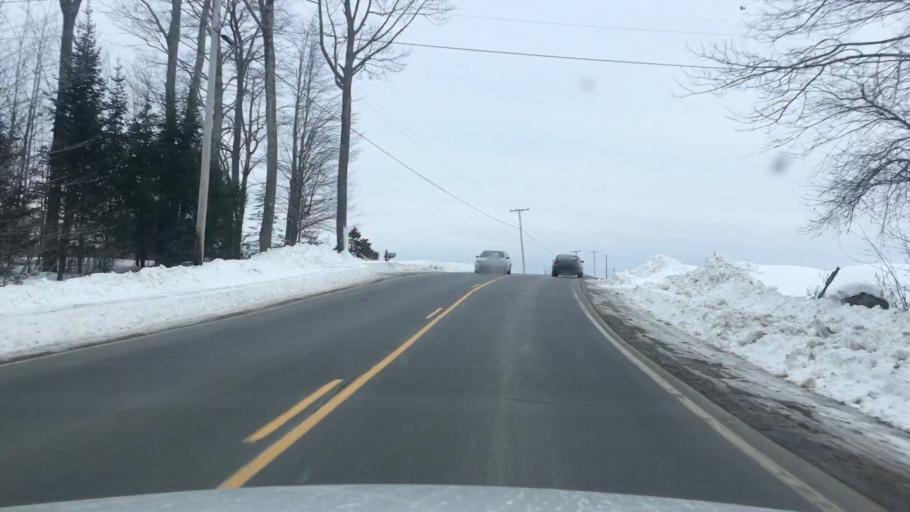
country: US
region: Maine
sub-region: Penobscot County
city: Garland
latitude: 44.9832
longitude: -69.0879
